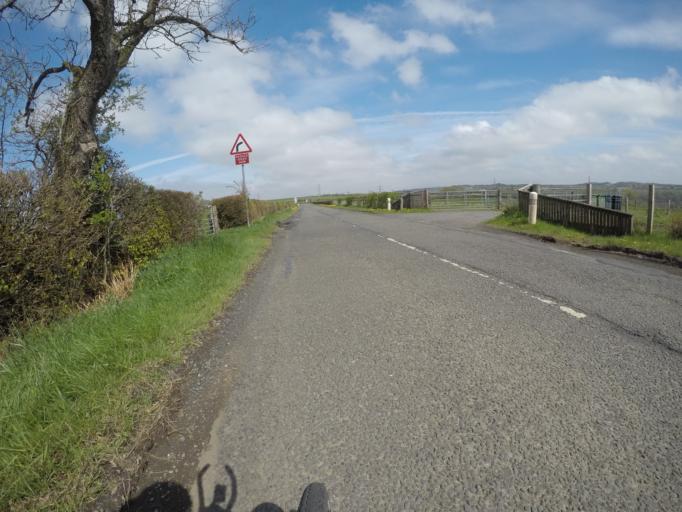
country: GB
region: Scotland
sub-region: East Ayrshire
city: Stewarton
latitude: 55.6998
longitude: -4.4839
